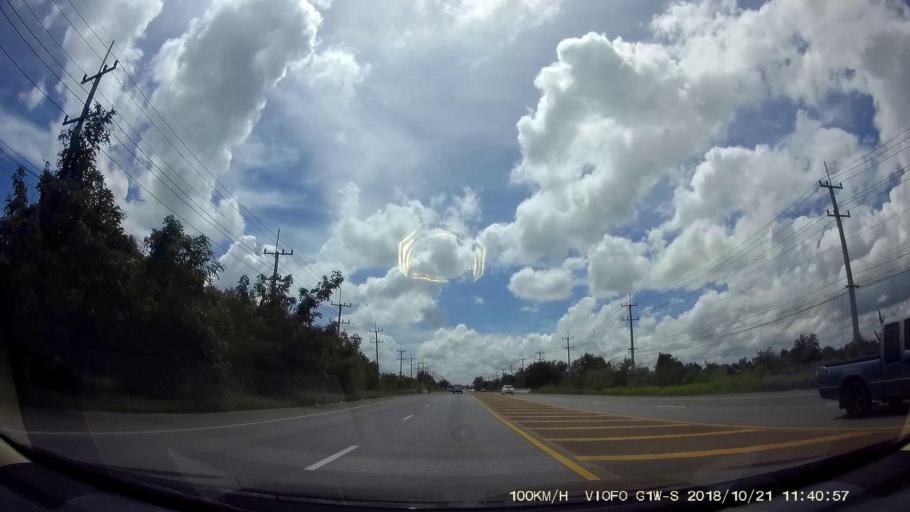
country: TH
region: Chaiyaphum
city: Chaiyaphum
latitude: 15.7062
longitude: 102.0152
